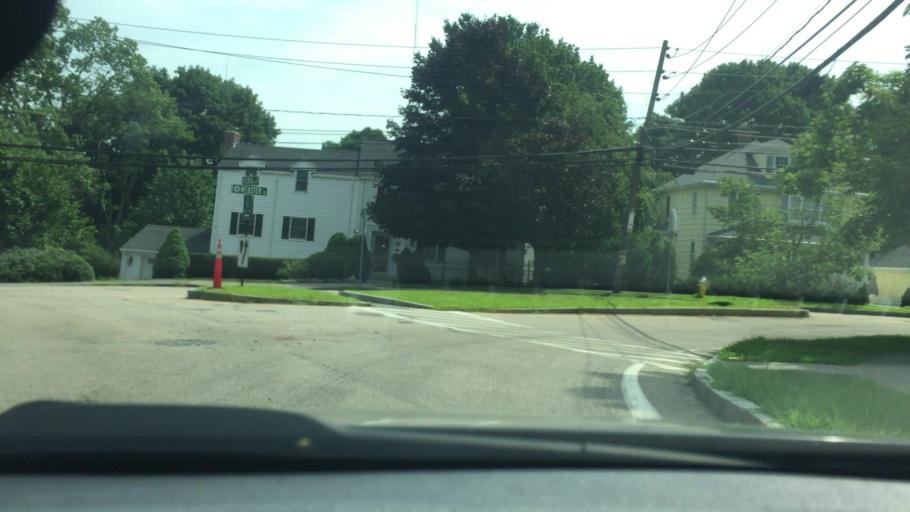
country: US
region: Massachusetts
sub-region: Norfolk County
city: Needham
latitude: 42.3068
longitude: -71.2367
